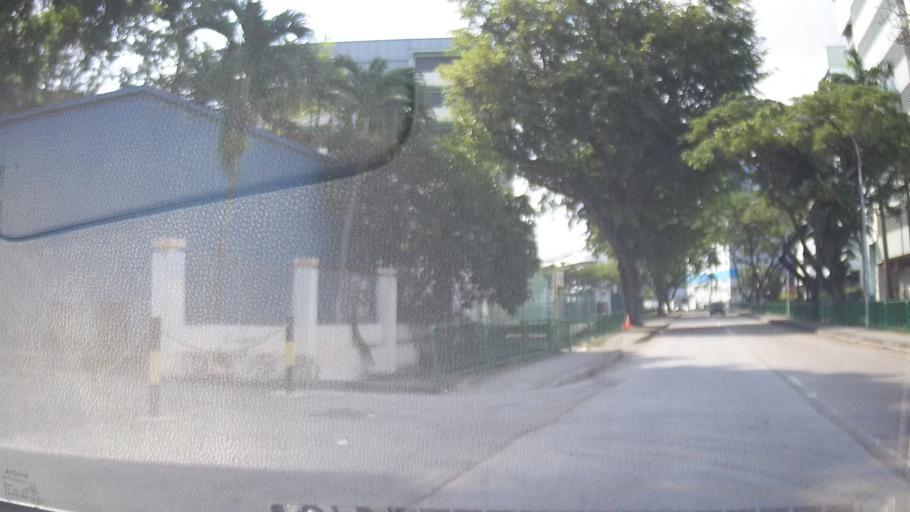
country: SG
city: Singapore
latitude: 1.3159
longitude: 103.8675
